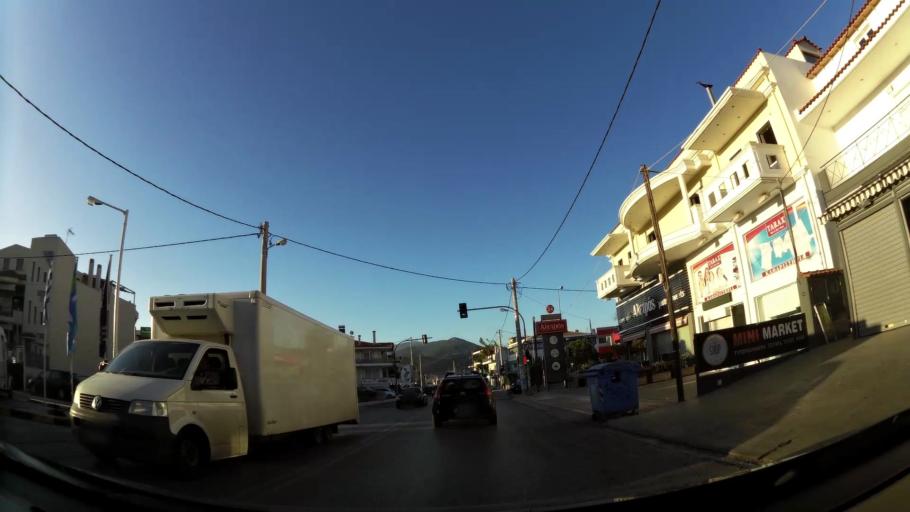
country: GR
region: Attica
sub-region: Nomarchia Anatolikis Attikis
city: Gerakas
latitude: 38.0251
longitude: 23.8494
